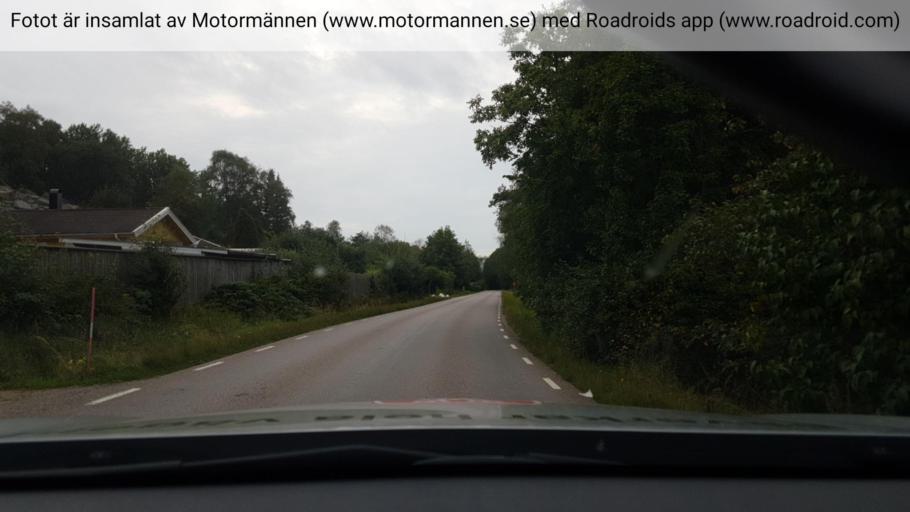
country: SE
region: Vaestra Goetaland
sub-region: Tanums Kommun
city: Grebbestad
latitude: 58.6346
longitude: 11.2878
